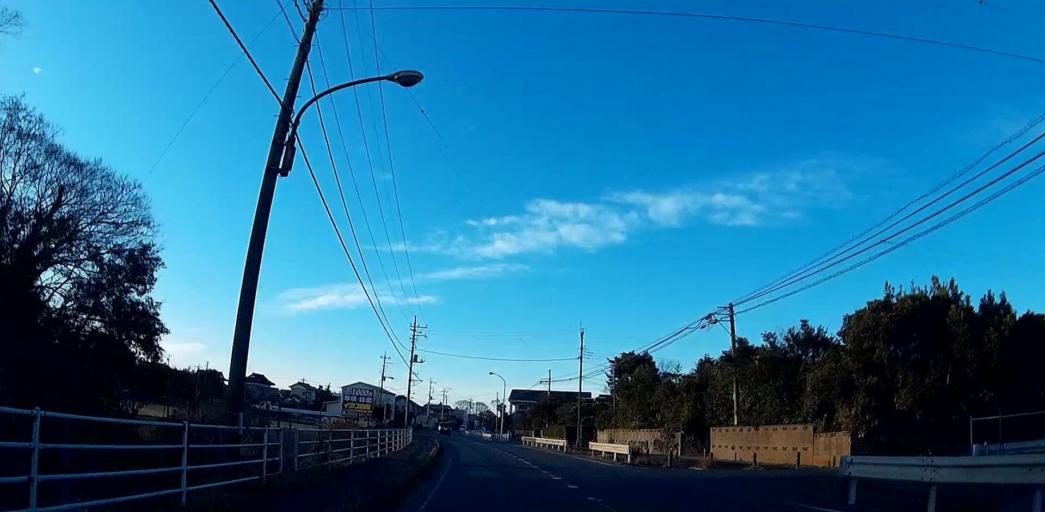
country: JP
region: Chiba
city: Omigawa
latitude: 35.8728
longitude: 140.5910
